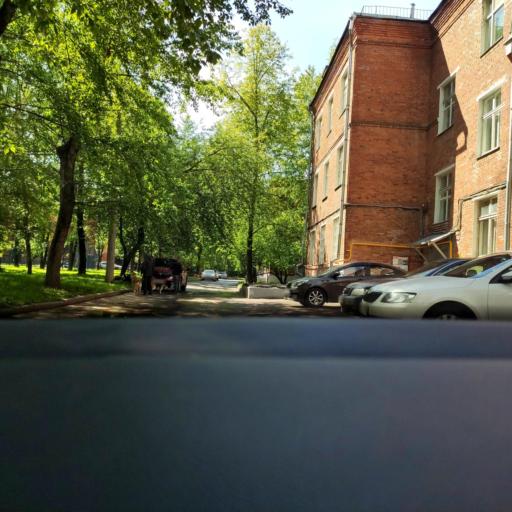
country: RU
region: Moscow
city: Altuf'yevskiy
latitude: 55.8823
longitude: 37.5775
